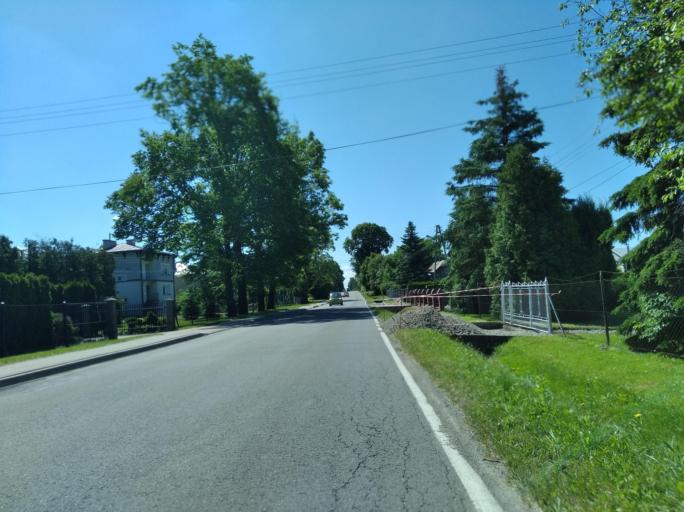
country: PL
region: Subcarpathian Voivodeship
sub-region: Powiat krosnienski
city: Chorkowka
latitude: 49.6625
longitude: 21.6925
